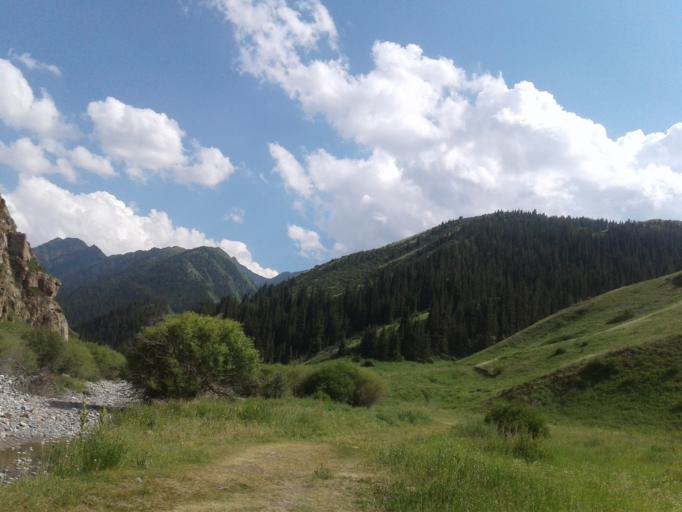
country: KG
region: Naryn
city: Naryn
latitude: 41.4584
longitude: 76.4529
